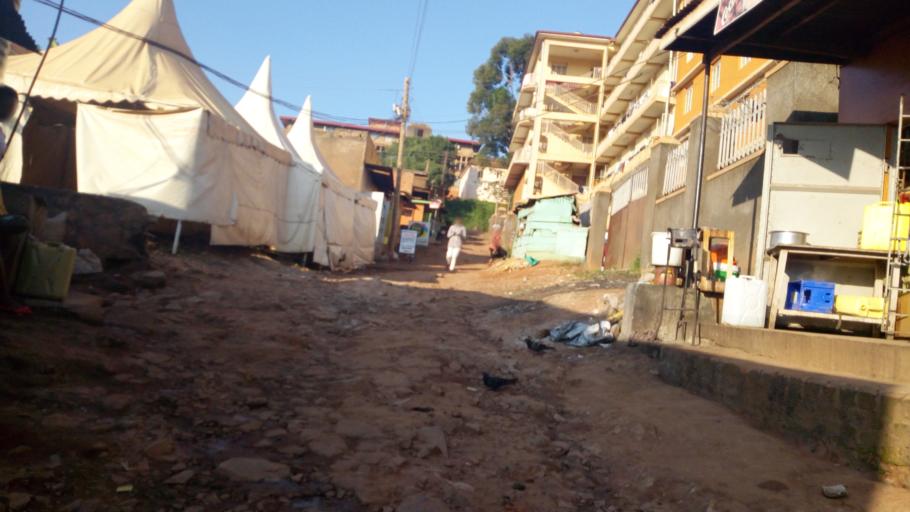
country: UG
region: Central Region
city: Kampala Central Division
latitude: 0.3362
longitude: 32.5628
